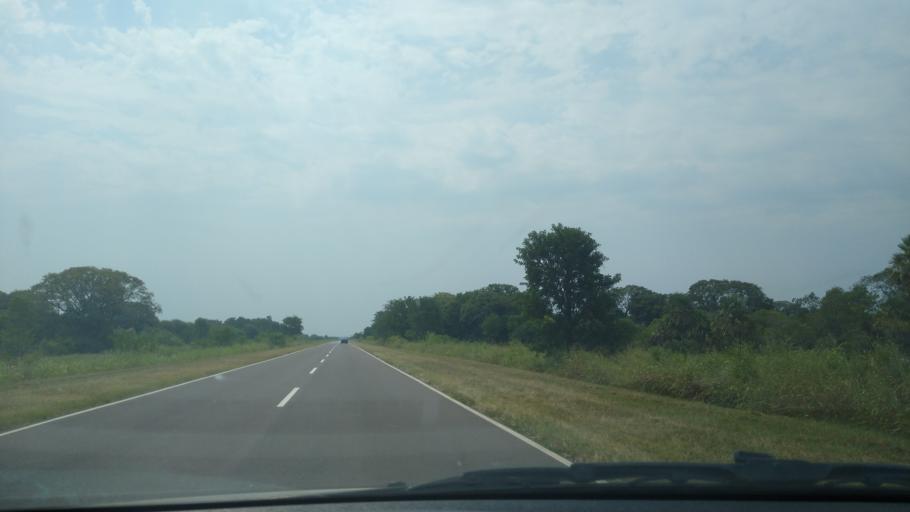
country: AR
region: Chaco
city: La Eduvigis
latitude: -27.0090
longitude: -58.9707
